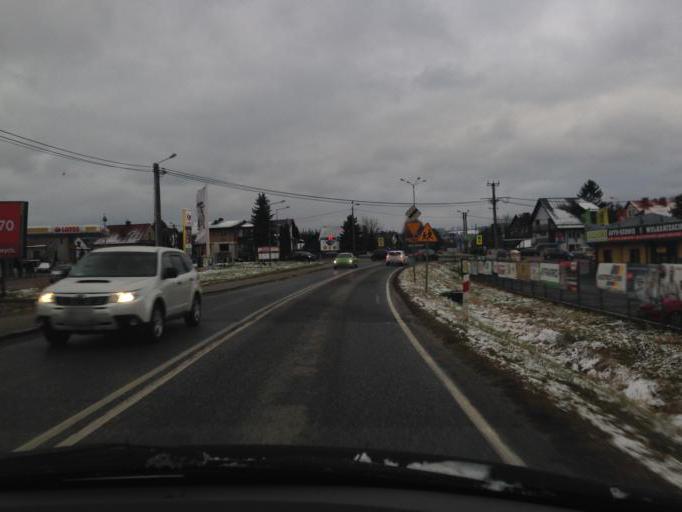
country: PL
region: Lesser Poland Voivodeship
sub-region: Powiat tarnowski
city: Zakliczyn
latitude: 49.8571
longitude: 20.8142
